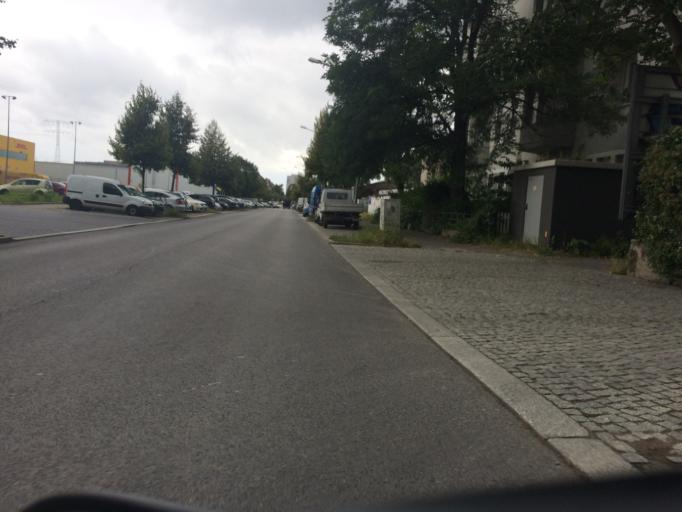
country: DE
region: Berlin
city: Lichtenberg
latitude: 52.5230
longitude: 13.4969
